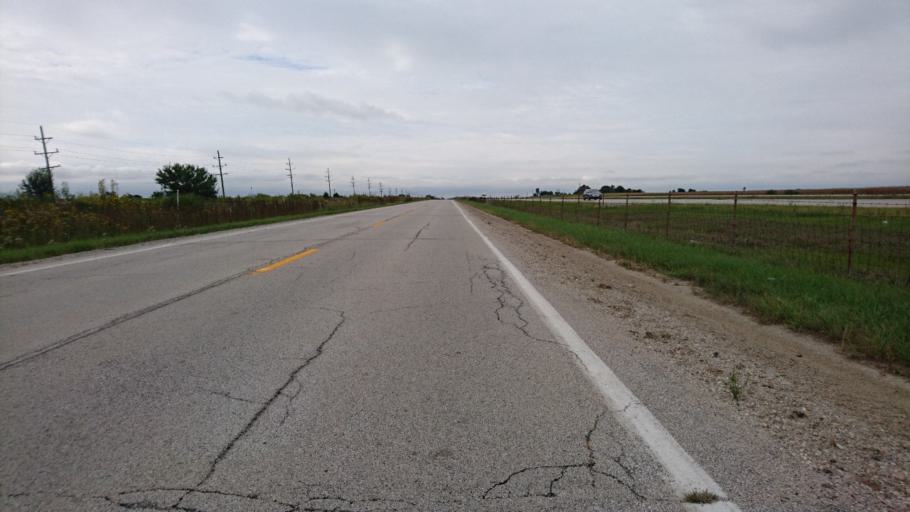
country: US
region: Illinois
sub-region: Livingston County
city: Odell
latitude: 41.0420
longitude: -88.4892
